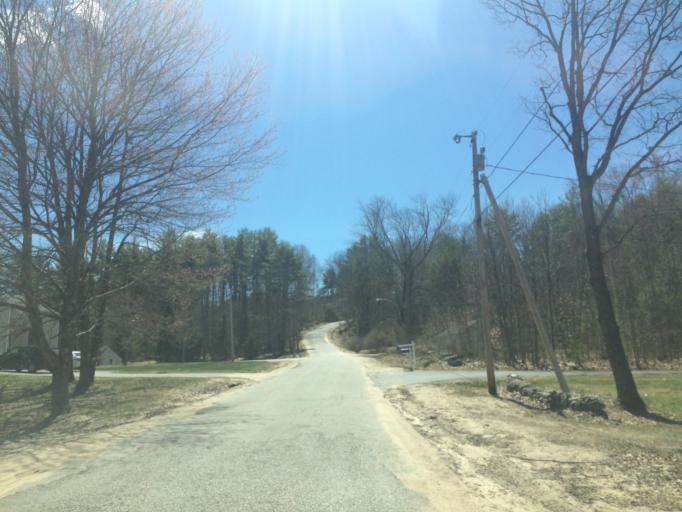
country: US
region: Maine
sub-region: Oxford County
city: Porter
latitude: 43.8053
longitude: -70.8741
